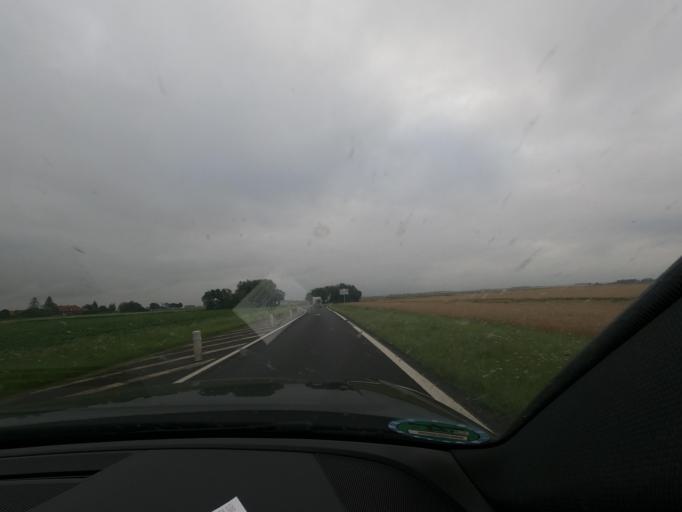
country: FR
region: Picardie
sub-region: Departement de la Somme
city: Rosieres-en-Santerre
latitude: 49.7457
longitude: 2.6686
